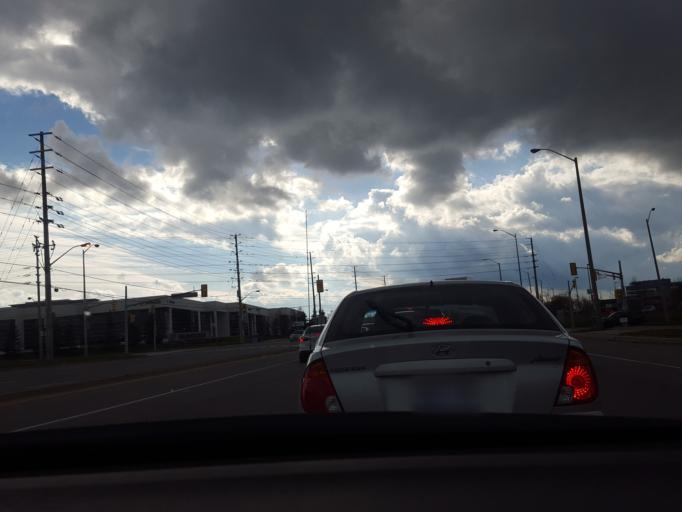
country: CA
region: Ontario
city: Brampton
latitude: 43.6147
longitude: -79.7442
